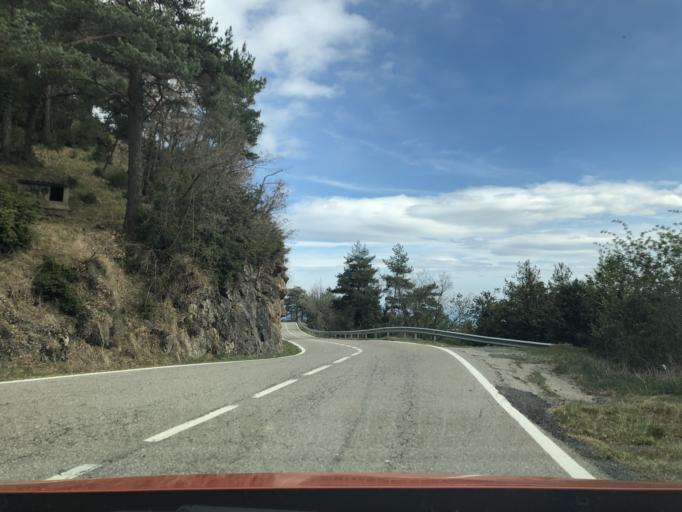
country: ES
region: Catalonia
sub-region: Provincia de Barcelona
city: Capolat
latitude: 42.0937
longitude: 1.7674
